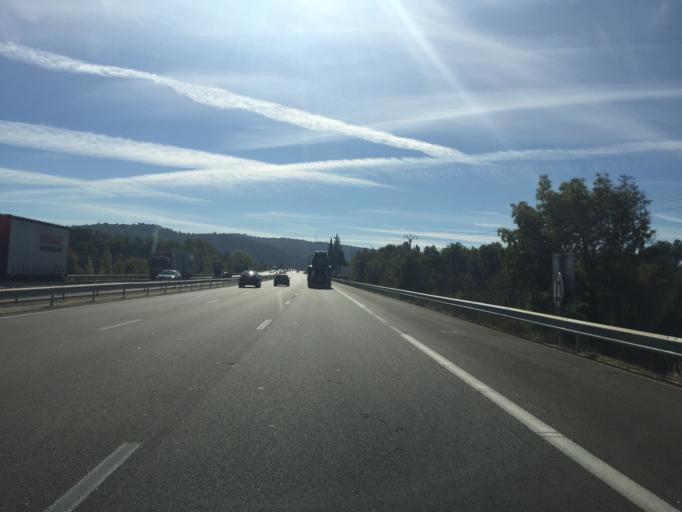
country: FR
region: Provence-Alpes-Cote d'Azur
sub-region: Departement des Bouches-du-Rhone
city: Lamanon
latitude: 43.7118
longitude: 5.0938
